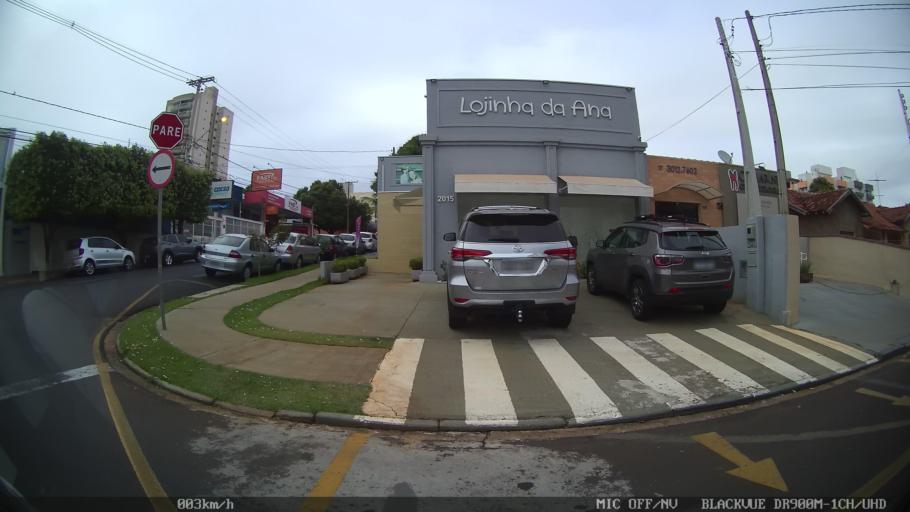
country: BR
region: Sao Paulo
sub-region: Sao Jose Do Rio Preto
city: Sao Jose do Rio Preto
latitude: -20.8336
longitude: -49.3910
